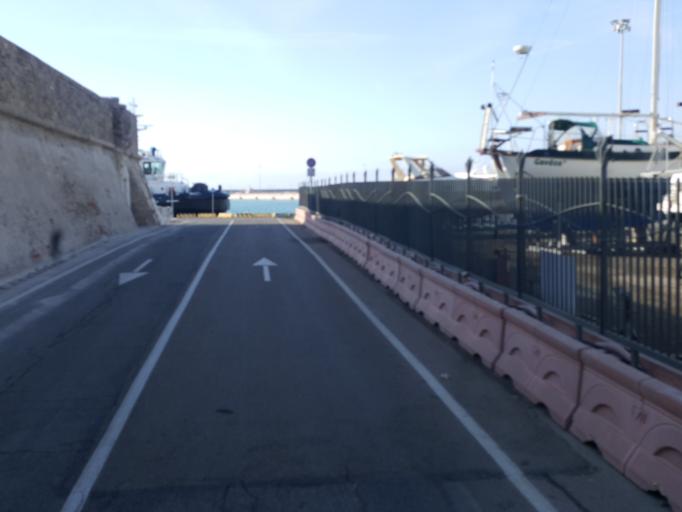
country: IT
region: Latium
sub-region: Citta metropolitana di Roma Capitale
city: Civitavecchia
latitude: 42.0947
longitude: 11.7870
